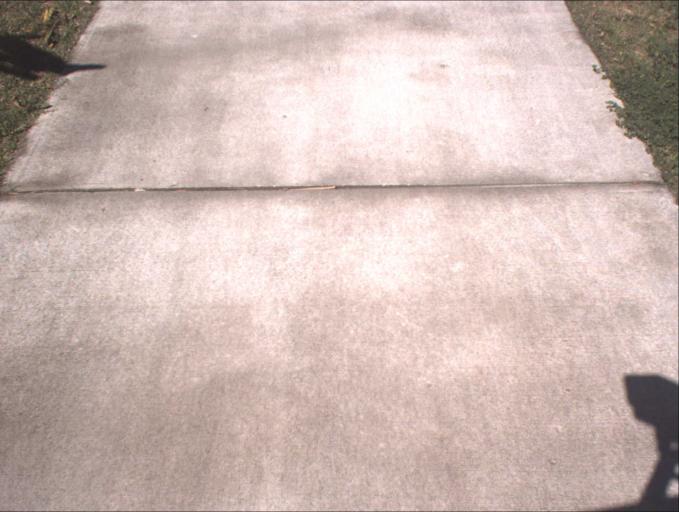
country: AU
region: Queensland
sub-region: Logan
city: Waterford West
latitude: -27.6777
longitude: 153.1078
